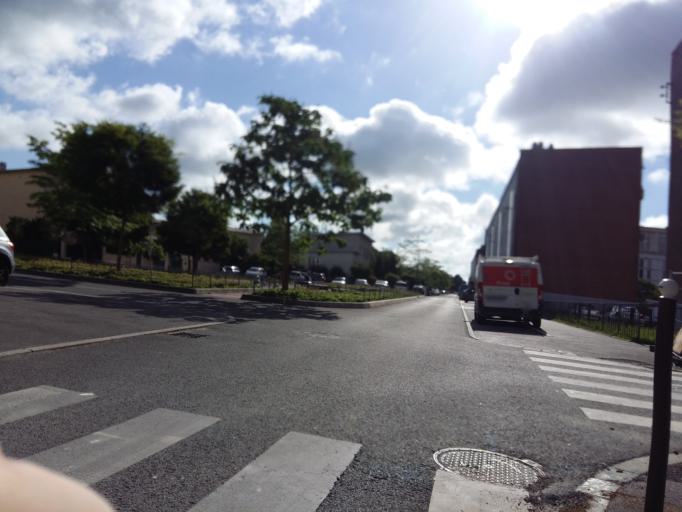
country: FR
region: Picardie
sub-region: Departement de la Somme
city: Amiens
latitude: 49.9136
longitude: 2.3044
